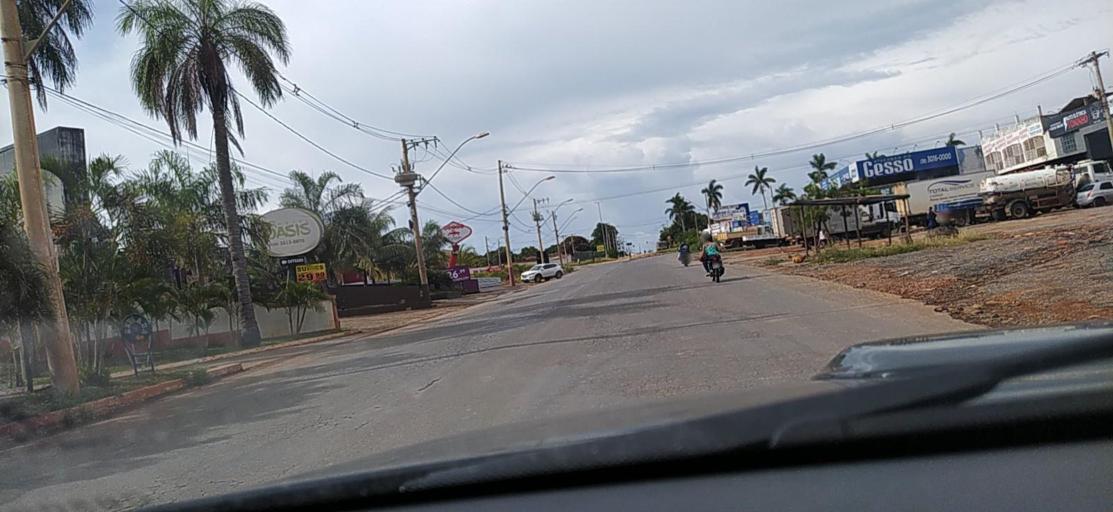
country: BR
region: Minas Gerais
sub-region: Montes Claros
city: Montes Claros
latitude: -16.7475
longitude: -43.8464
